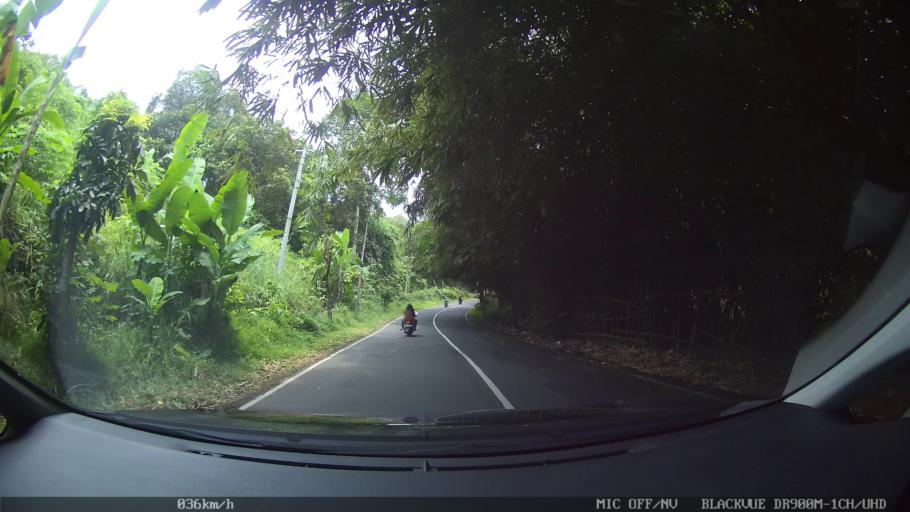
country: ID
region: Lampung
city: Bandarlampung
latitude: -5.4244
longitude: 105.2364
